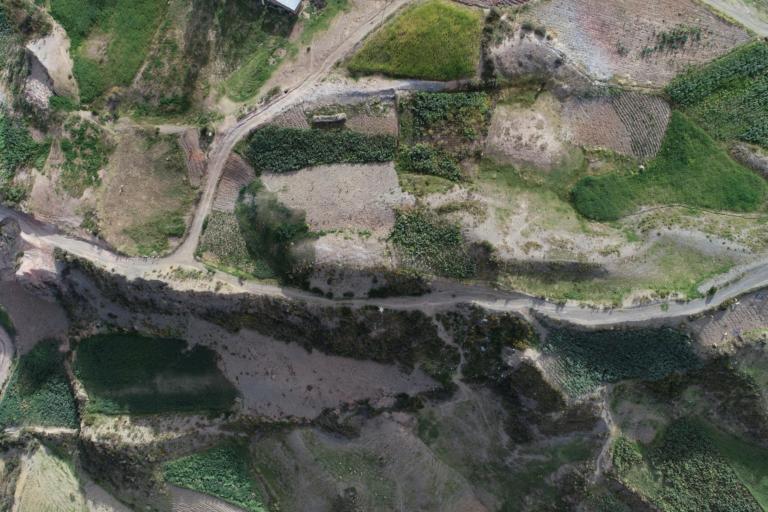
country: BO
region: La Paz
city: La Paz
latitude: -16.5486
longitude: -68.0001
